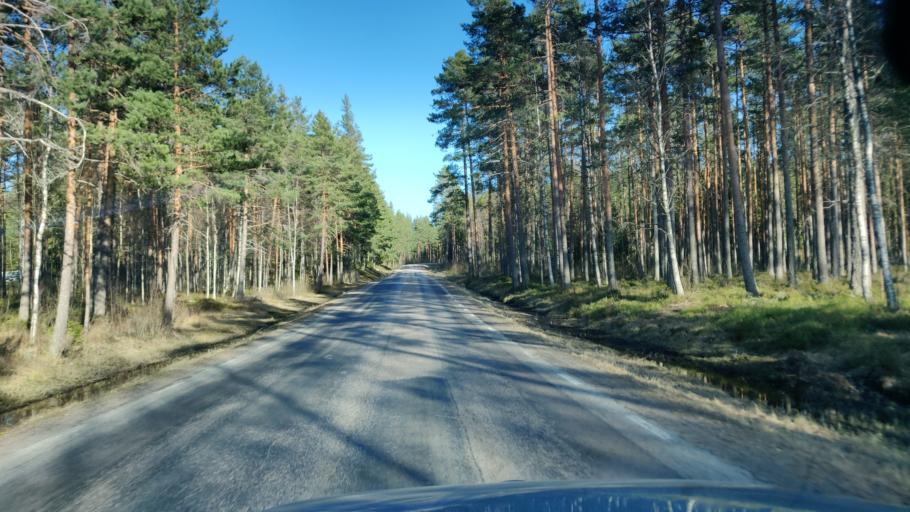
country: SE
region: Vaermland
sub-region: Sunne Kommun
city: Sunne
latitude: 59.9930
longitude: 13.2999
